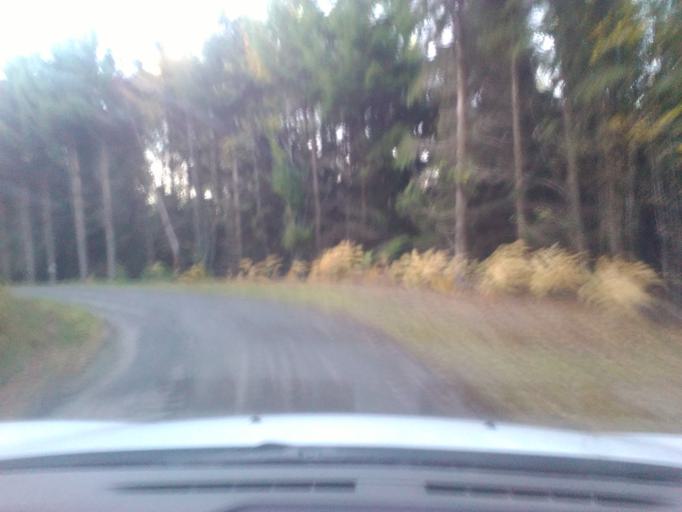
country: FR
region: Lorraine
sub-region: Departement des Vosges
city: Jeanmenil
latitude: 48.2826
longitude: 6.7381
